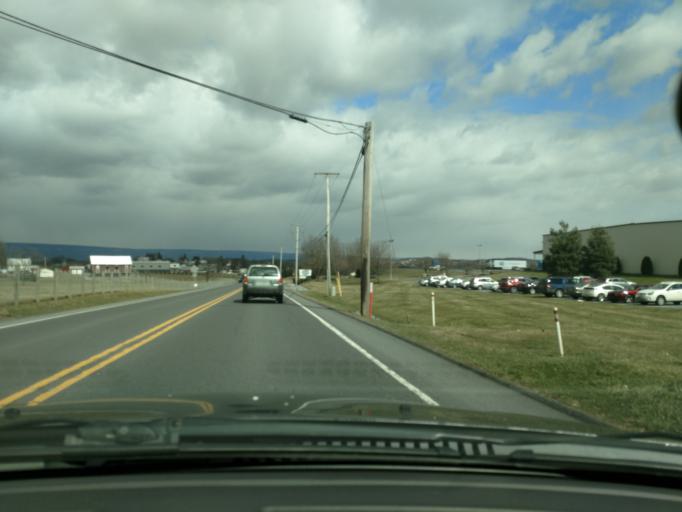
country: US
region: Pennsylvania
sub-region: Lebanon County
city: Myerstown
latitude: 40.4115
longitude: -76.3021
